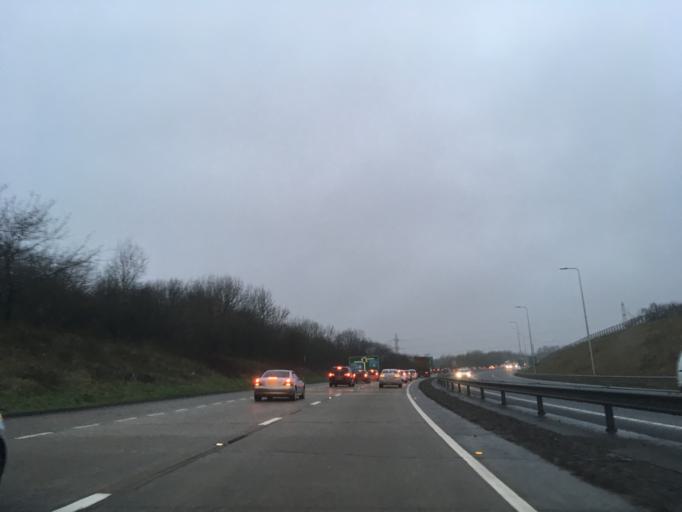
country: GB
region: Wales
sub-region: Cardiff
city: Pentyrch
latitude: 51.5024
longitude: -3.3054
